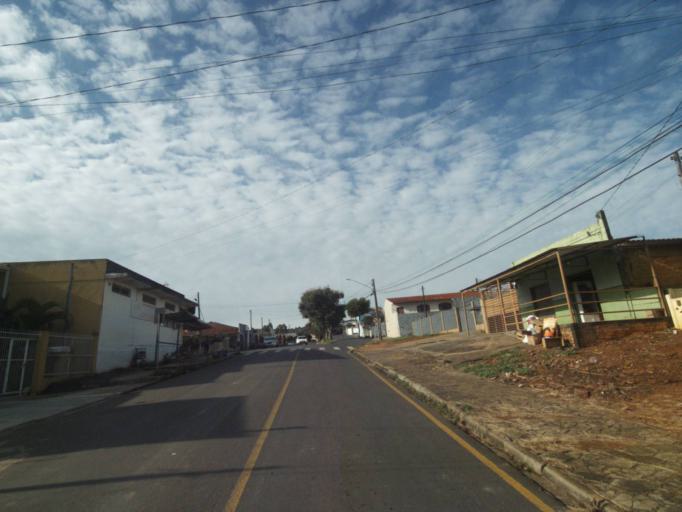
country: BR
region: Parana
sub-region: Telemaco Borba
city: Telemaco Borba
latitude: -24.3459
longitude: -50.6123
